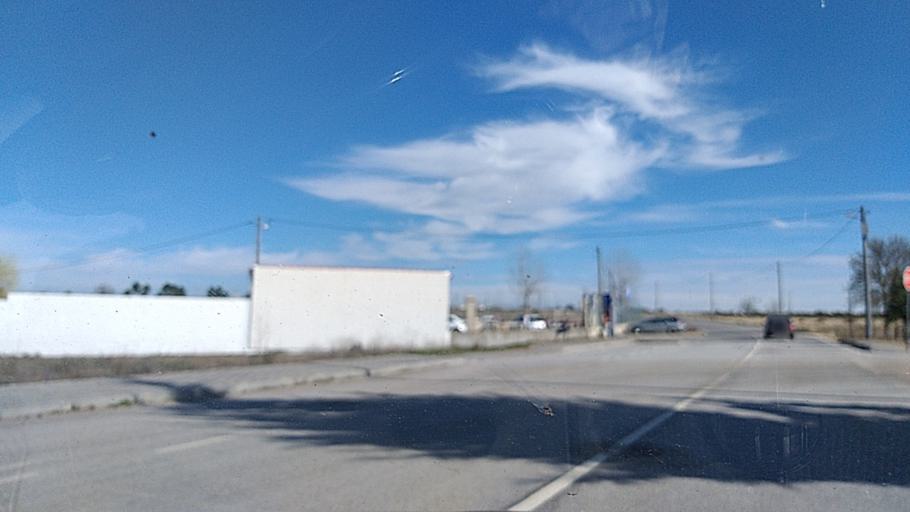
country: ES
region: Castille and Leon
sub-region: Provincia de Salamanca
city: Fuentes de Onoro
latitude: 40.5938
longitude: -6.9911
